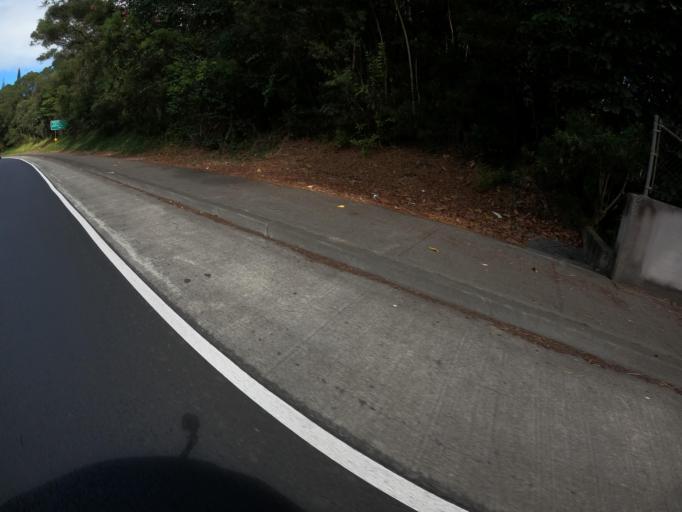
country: US
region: Hawaii
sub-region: Honolulu County
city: Kane'ohe
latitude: 21.4092
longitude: -157.8073
